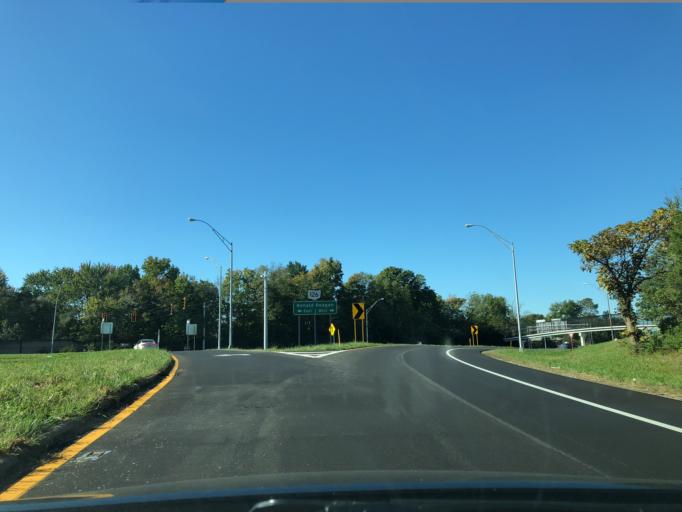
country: US
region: Ohio
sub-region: Hamilton County
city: Blue Ash
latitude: 39.2267
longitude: -84.3680
